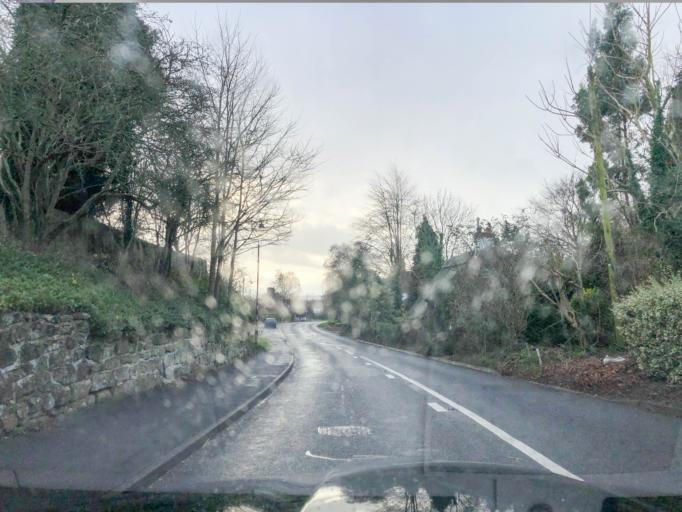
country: GB
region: England
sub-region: Warwickshire
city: Warwick
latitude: 52.3156
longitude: -1.5767
